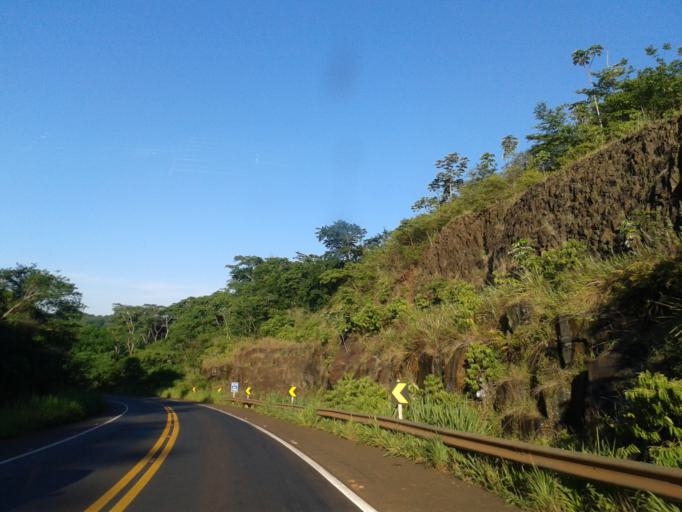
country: BR
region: Minas Gerais
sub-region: Ituiutaba
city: Ituiutaba
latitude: -18.9340
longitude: -49.7951
